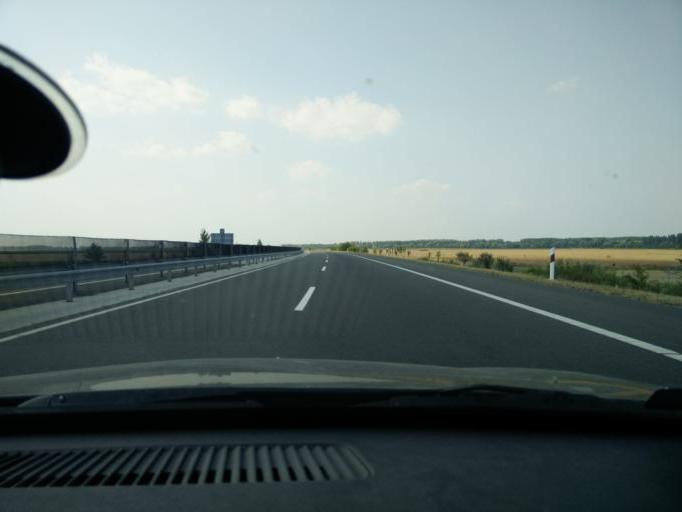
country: HU
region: Tolna
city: Ocseny
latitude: 46.3494
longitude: 18.7580
